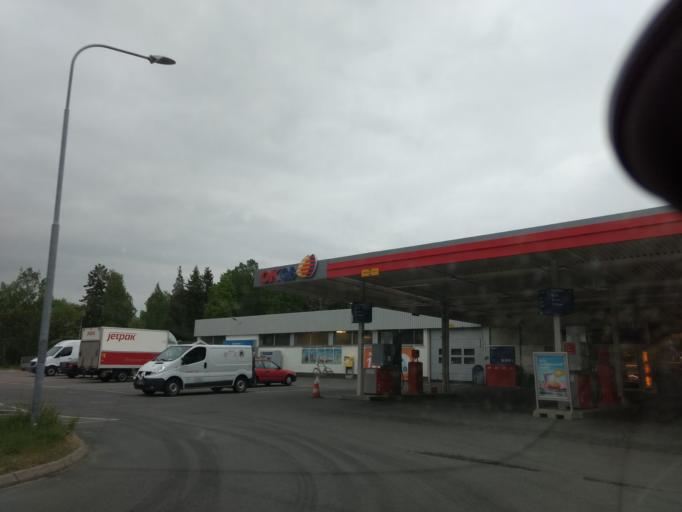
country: SE
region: Uppsala
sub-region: Uppsala Kommun
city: Uppsala
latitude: 59.8168
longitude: 17.6189
